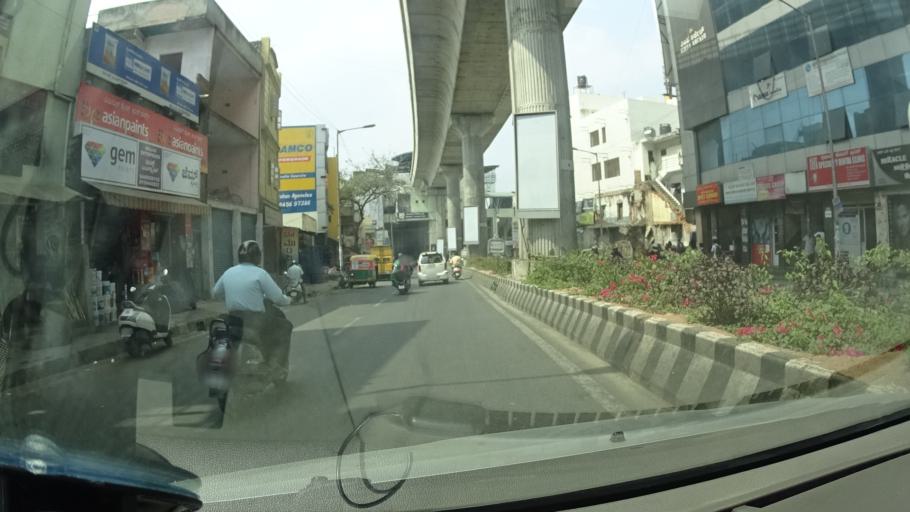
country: IN
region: Karnataka
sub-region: Bangalore Urban
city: Bangalore
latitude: 12.9981
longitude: 77.5586
